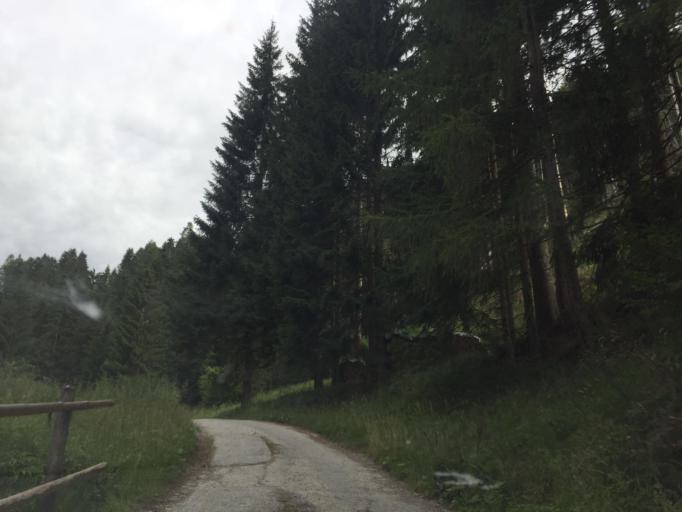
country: IT
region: Friuli Venezia Giulia
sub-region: Provincia di Udine
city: Forni Avoltri
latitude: 46.5813
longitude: 12.8107
